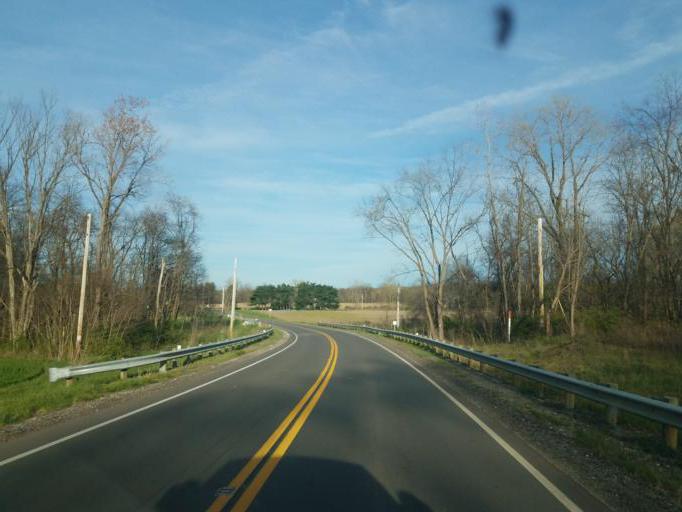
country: US
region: Ohio
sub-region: Crawford County
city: Crestline
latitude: 40.6995
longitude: -82.6934
